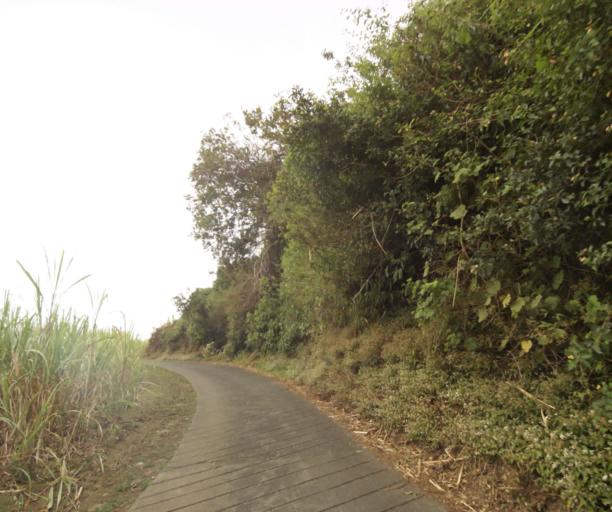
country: RE
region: Reunion
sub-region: Reunion
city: Saint-Paul
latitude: -21.0260
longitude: 55.3225
